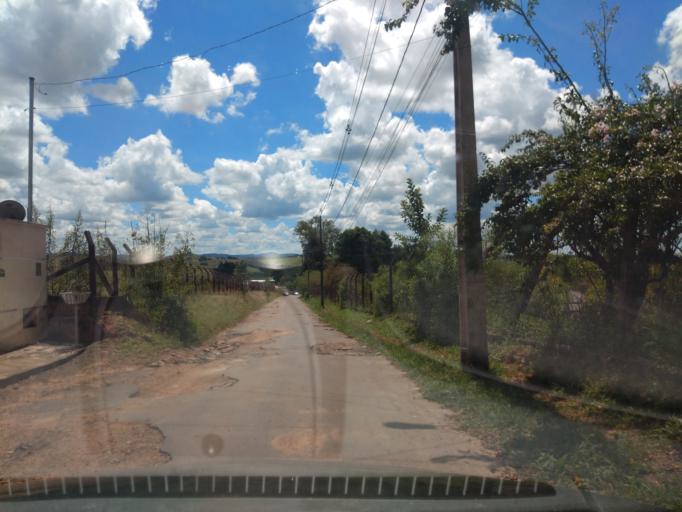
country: BR
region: Minas Gerais
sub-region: Tres Coracoes
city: Tres Coracoes
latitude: -21.6848
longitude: -45.2402
